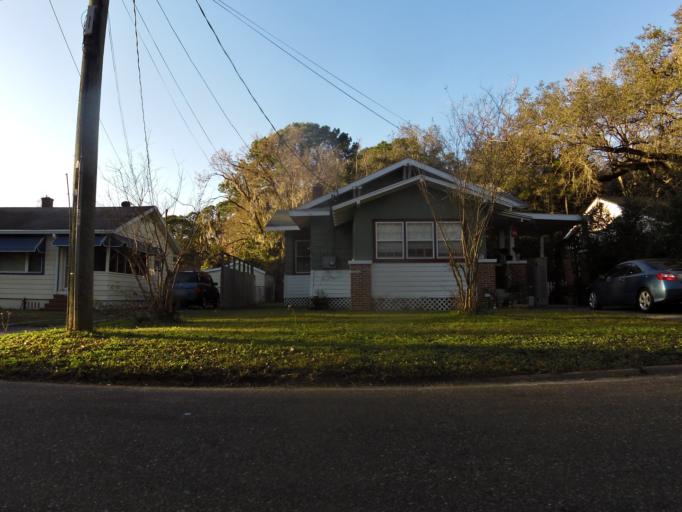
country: US
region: Florida
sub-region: Duval County
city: Jacksonville
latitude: 30.3172
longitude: -81.7206
